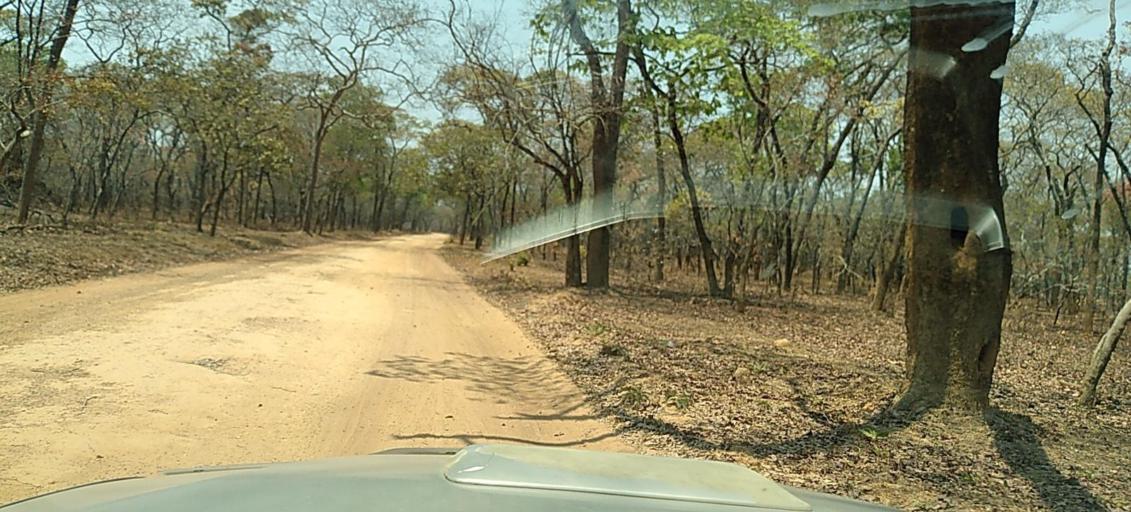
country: ZM
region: North-Western
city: Kasempa
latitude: -13.6073
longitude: 26.1781
